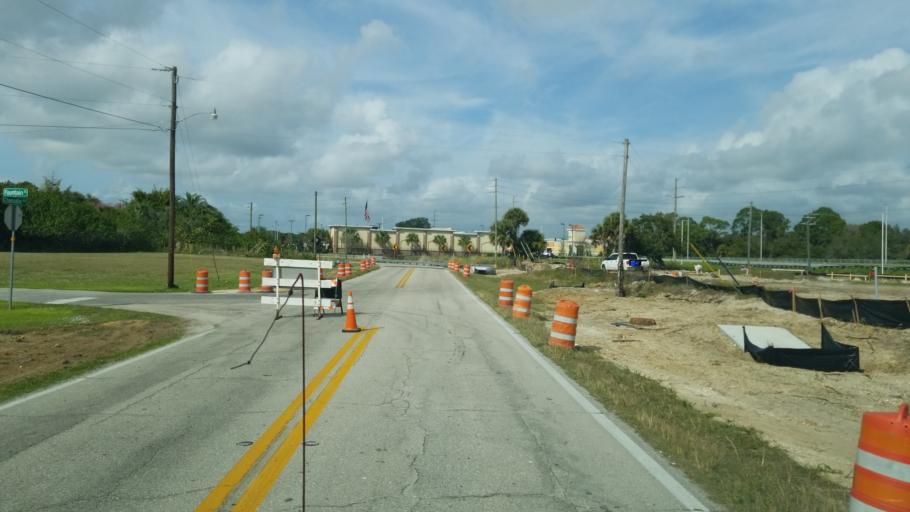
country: US
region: Florida
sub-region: Sarasota County
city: North Port
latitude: 27.0323
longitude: -82.2062
